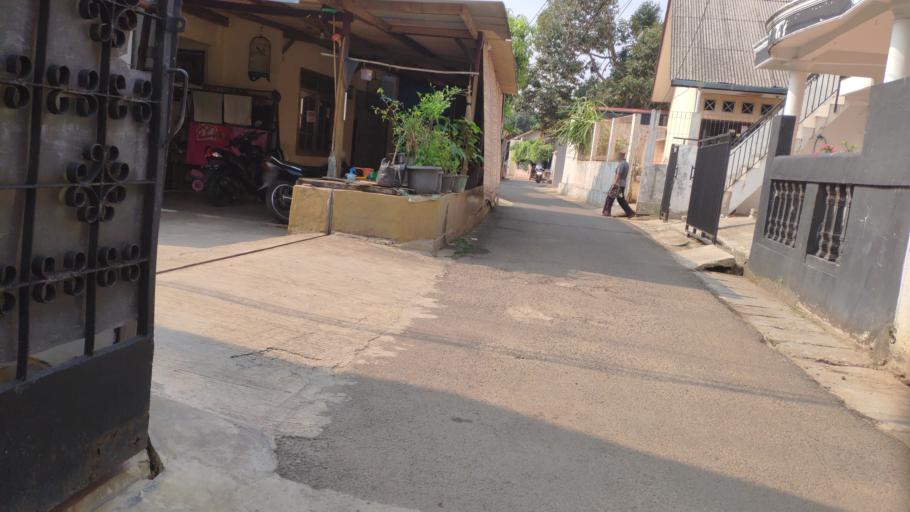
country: ID
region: West Java
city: Depok
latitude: -6.3251
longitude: 106.8136
